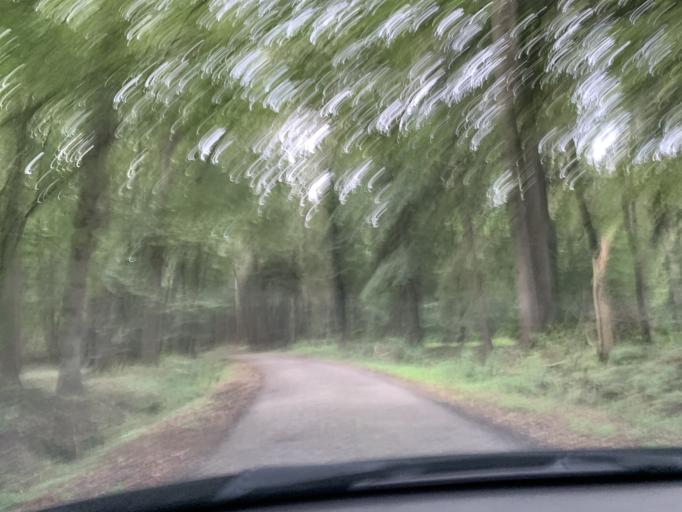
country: DE
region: Lower Saxony
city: Westerstede
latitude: 53.2679
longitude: 7.9981
